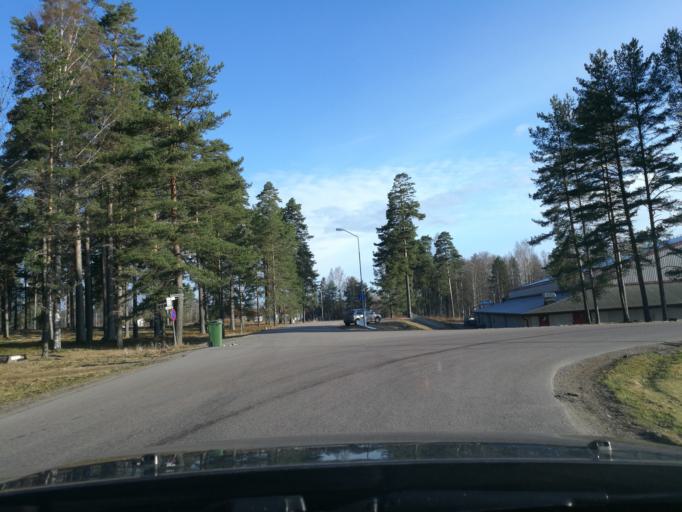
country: SE
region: Vaermland
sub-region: Eda Kommun
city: Charlottenberg
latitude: 59.8787
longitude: 12.2837
